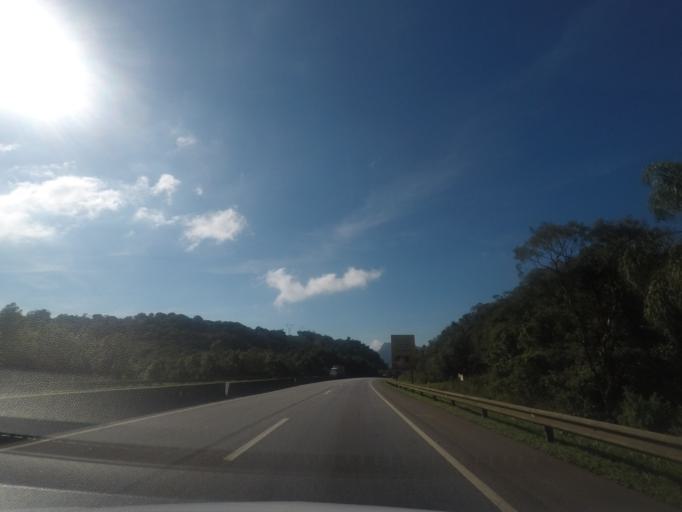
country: BR
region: Parana
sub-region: Piraquara
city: Piraquara
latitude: -25.5899
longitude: -48.9333
